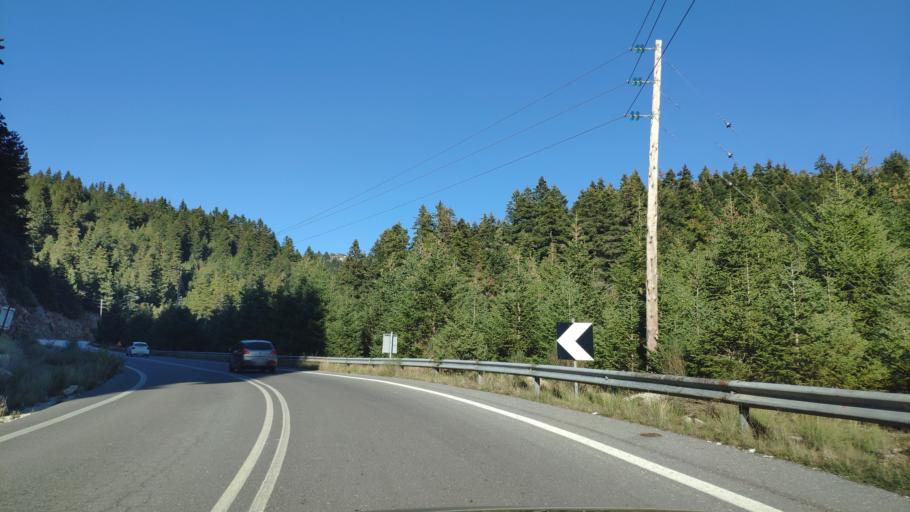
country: GR
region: Peloponnese
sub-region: Nomos Arkadias
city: Dimitsana
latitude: 37.6395
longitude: 22.0971
